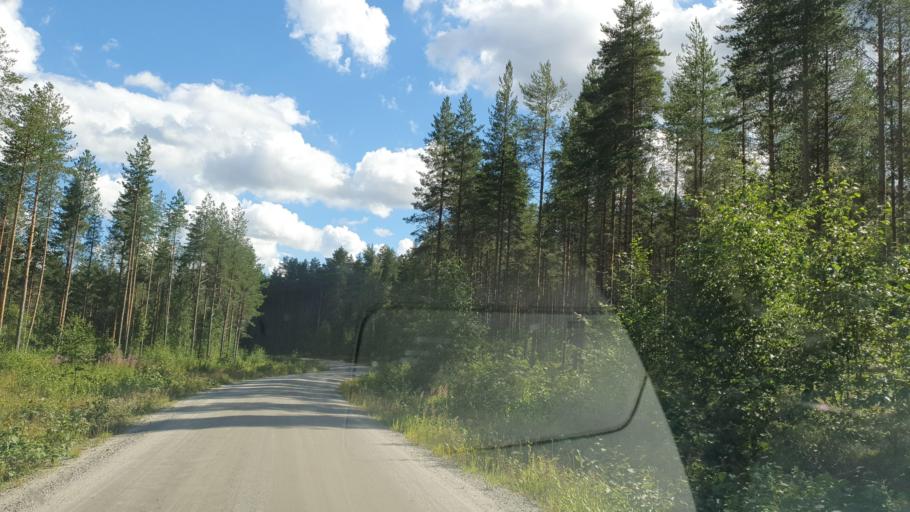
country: FI
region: Kainuu
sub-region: Kehys-Kainuu
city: Kuhmo
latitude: 64.0998
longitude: 29.4040
